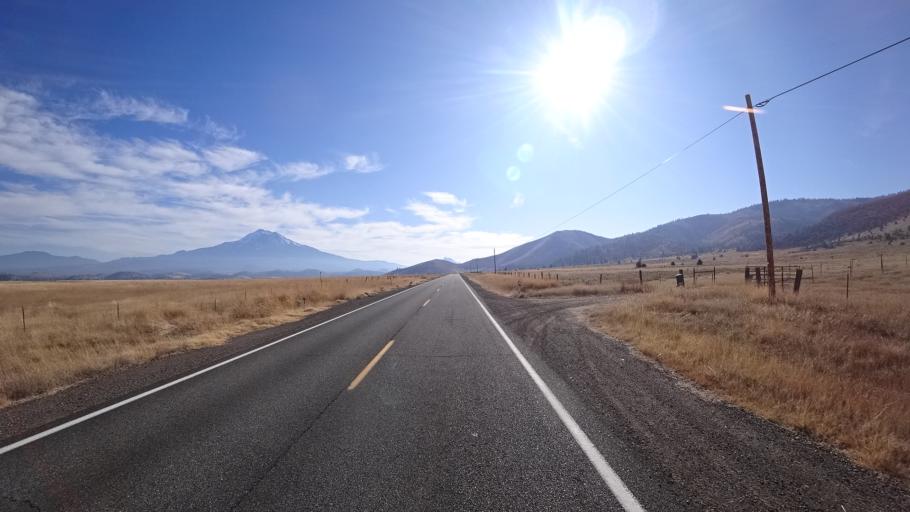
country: US
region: California
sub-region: Siskiyou County
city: Weed
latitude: 41.4837
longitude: -122.4973
